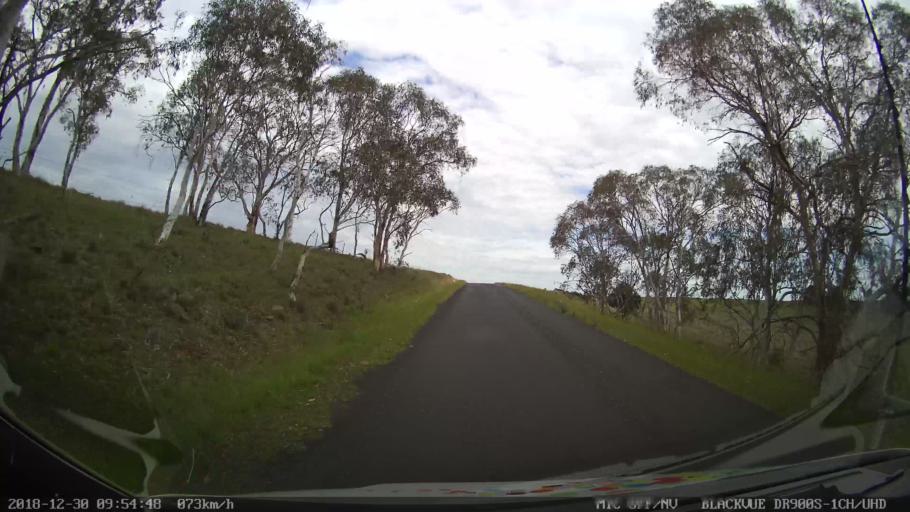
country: AU
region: New South Wales
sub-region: Cooma-Monaro
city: Cooma
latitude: -36.5190
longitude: 149.2731
